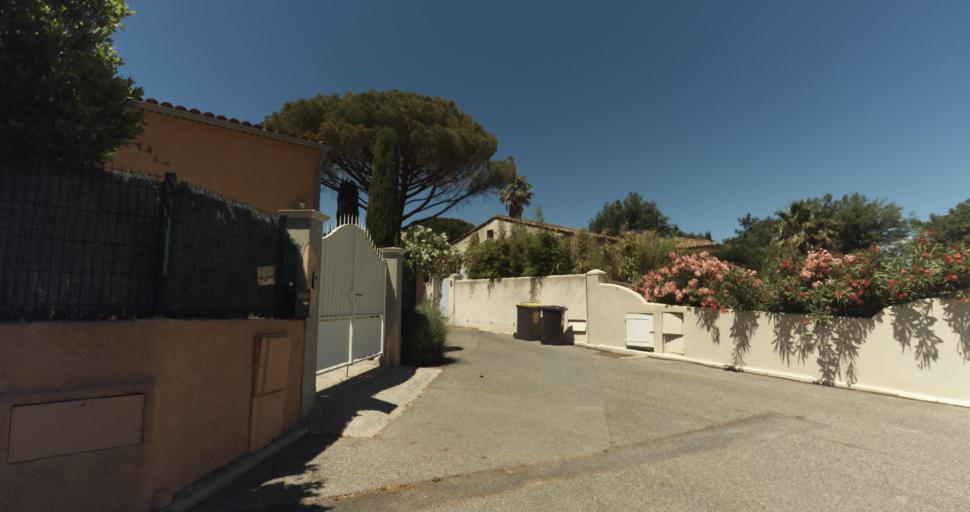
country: FR
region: Provence-Alpes-Cote d'Azur
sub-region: Departement du Var
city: Gassin
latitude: 43.2446
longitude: 6.5689
